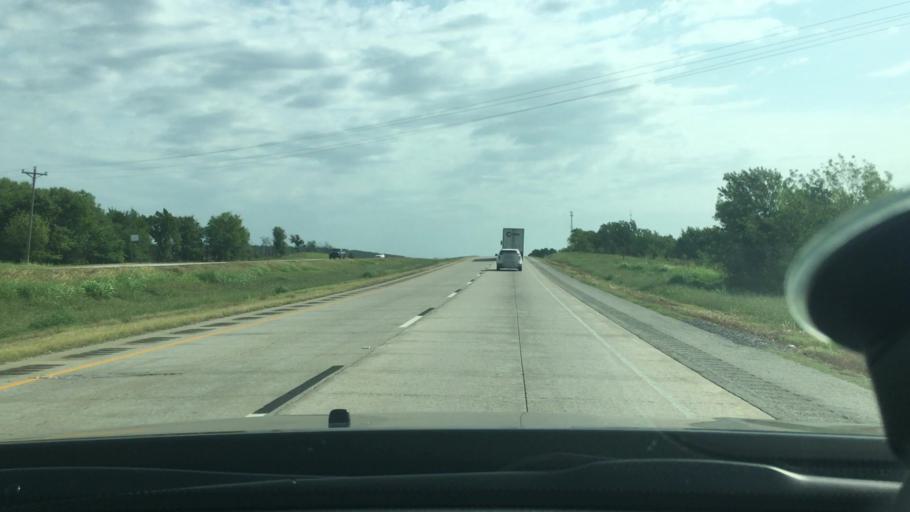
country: US
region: Oklahoma
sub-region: Atoka County
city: Atoka
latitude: 34.4230
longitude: -96.0931
